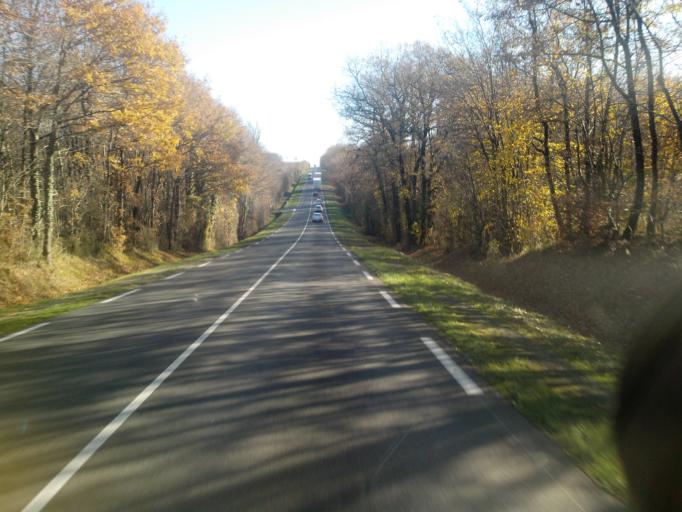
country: FR
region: Poitou-Charentes
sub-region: Departement de la Vienne
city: Terce
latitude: 46.4286
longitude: 0.6166
